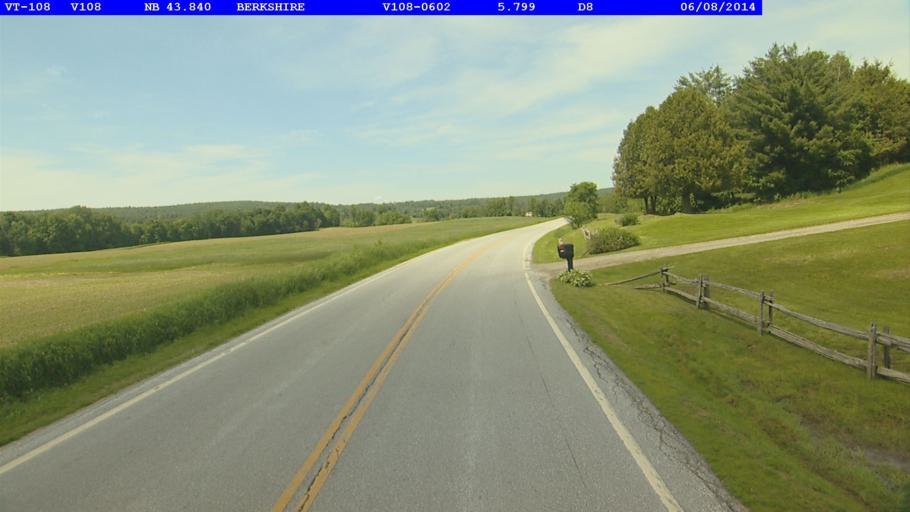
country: US
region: Vermont
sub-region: Franklin County
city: Enosburg Falls
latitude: 45.0006
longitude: -72.8251
